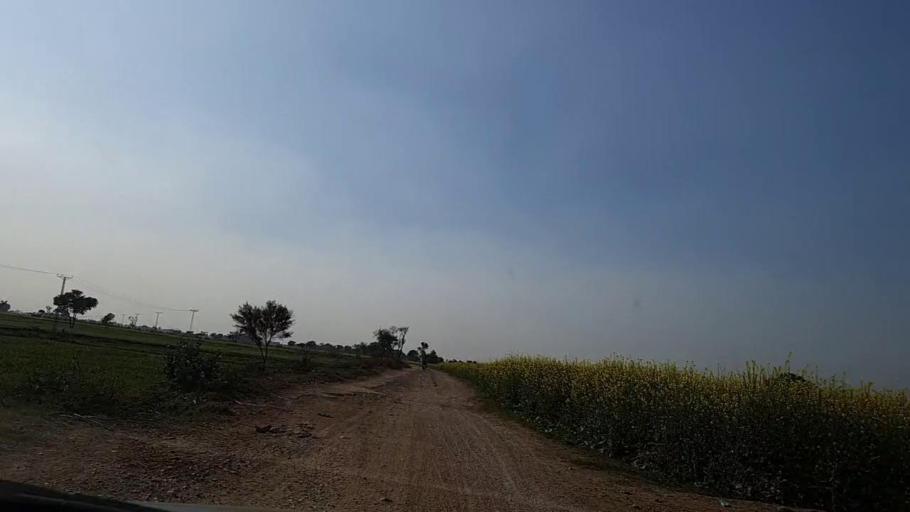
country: PK
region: Sindh
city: Sakrand
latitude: 26.1281
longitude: 68.2651
